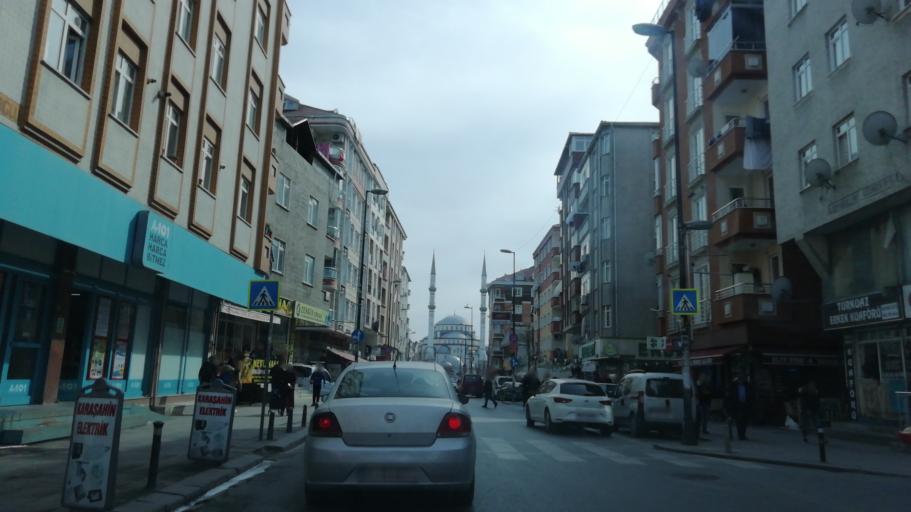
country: TR
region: Istanbul
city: Bahcelievler
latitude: 41.0120
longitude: 28.8390
